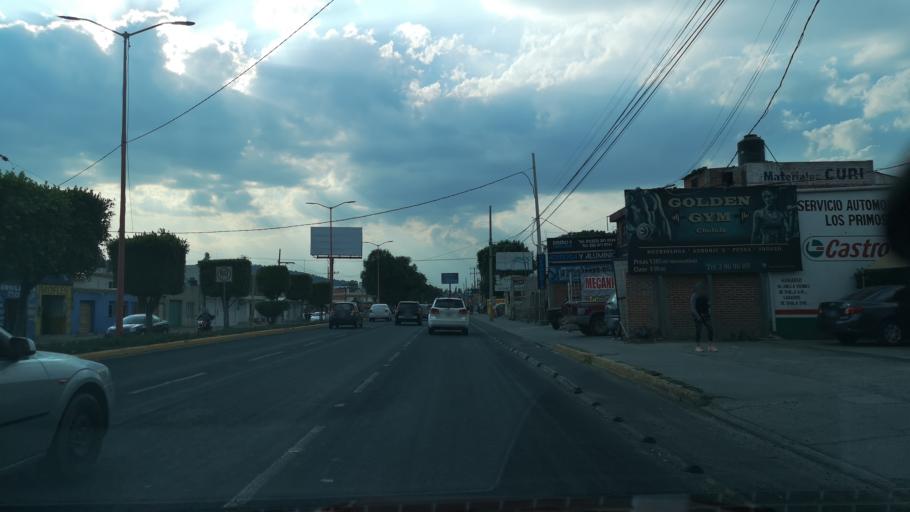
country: MX
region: Puebla
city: Cholula
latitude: 19.0698
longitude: -98.3114
